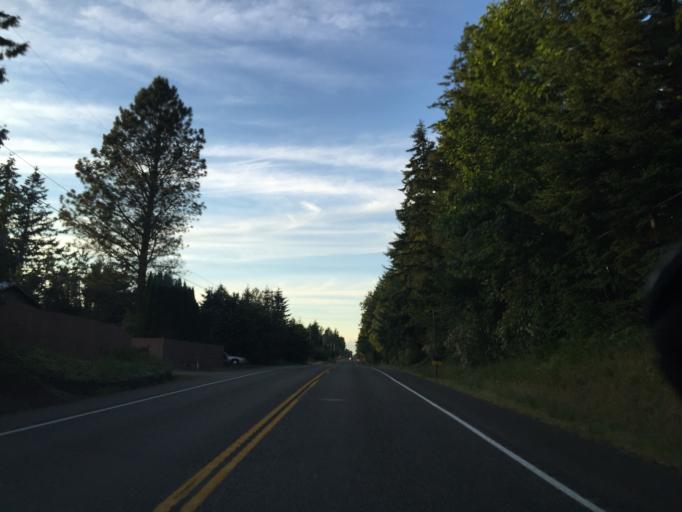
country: US
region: Washington
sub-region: Whatcom County
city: Geneva
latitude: 48.8273
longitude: -122.3768
